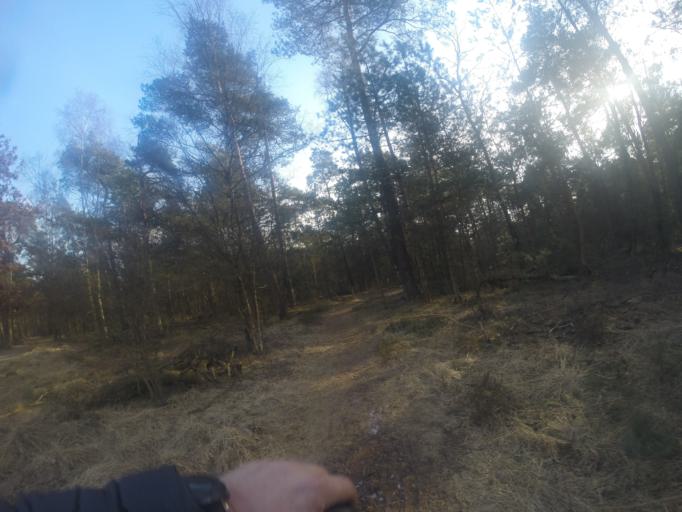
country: NL
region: Gelderland
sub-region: Gemeente Lochem
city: Almen
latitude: 52.1333
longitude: 6.3457
